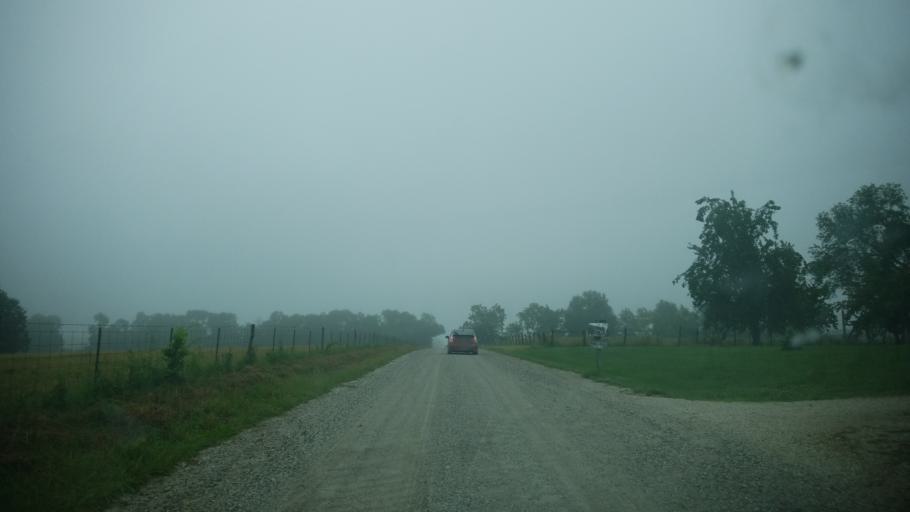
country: US
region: Missouri
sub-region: Audrain County
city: Vandalia
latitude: 39.3092
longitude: -91.3439
